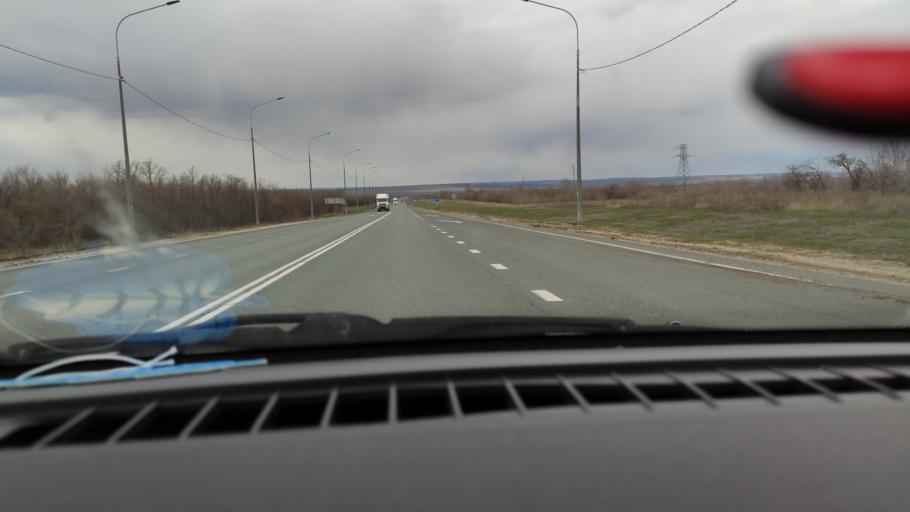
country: RU
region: Saratov
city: Yelshanka
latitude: 51.8262
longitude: 46.2826
